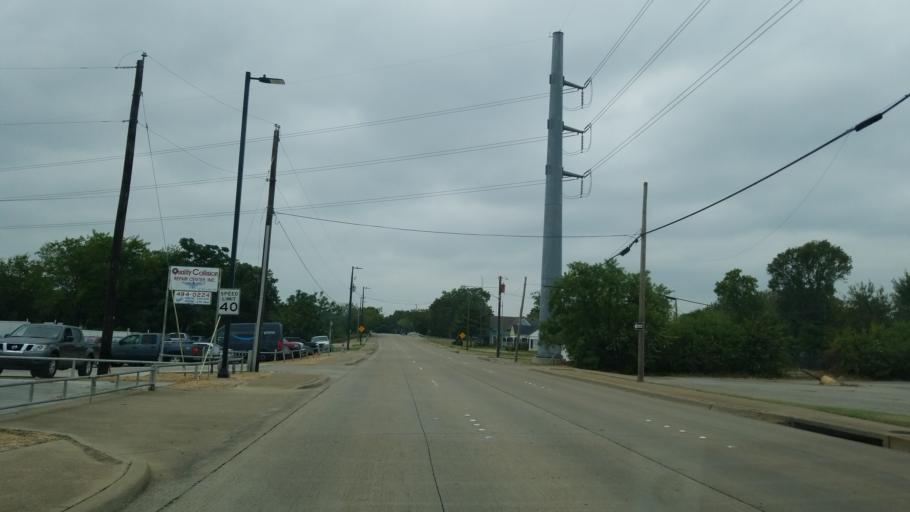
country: US
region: Texas
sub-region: Dallas County
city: Garland
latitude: 32.9110
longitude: -96.6489
